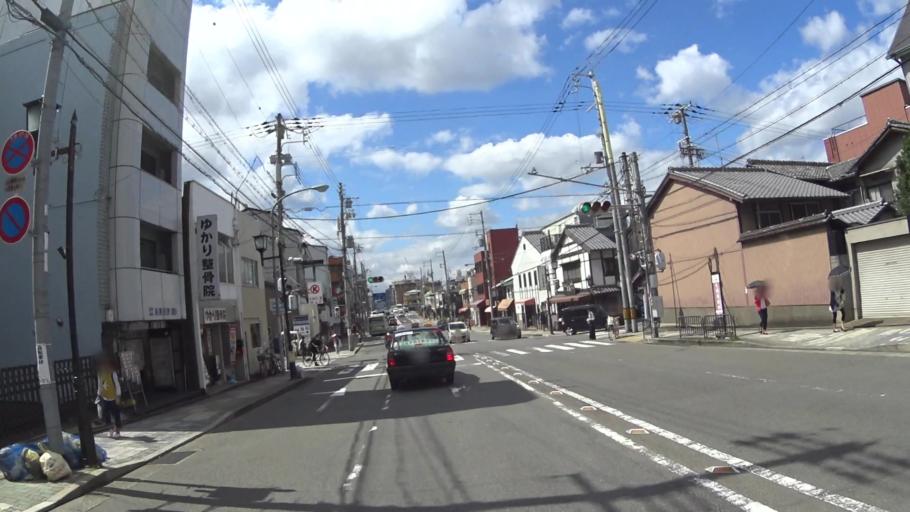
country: JP
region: Kyoto
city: Kyoto
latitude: 34.9893
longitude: 135.7700
